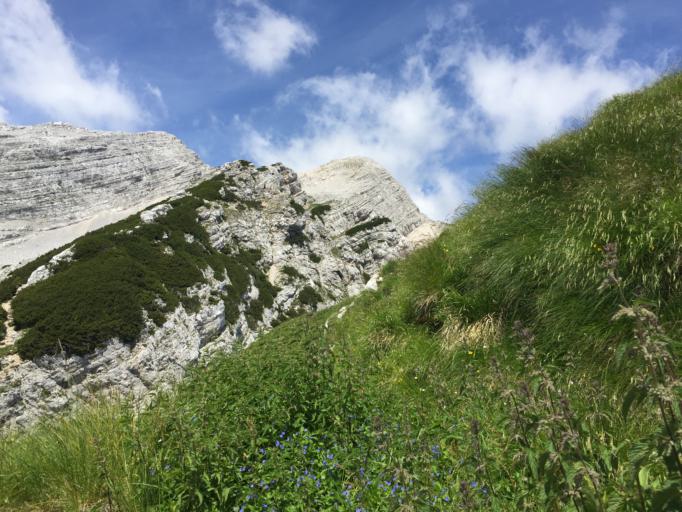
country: SI
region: Kranjska Gora
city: Kranjska Gora
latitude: 46.4301
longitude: 13.7369
